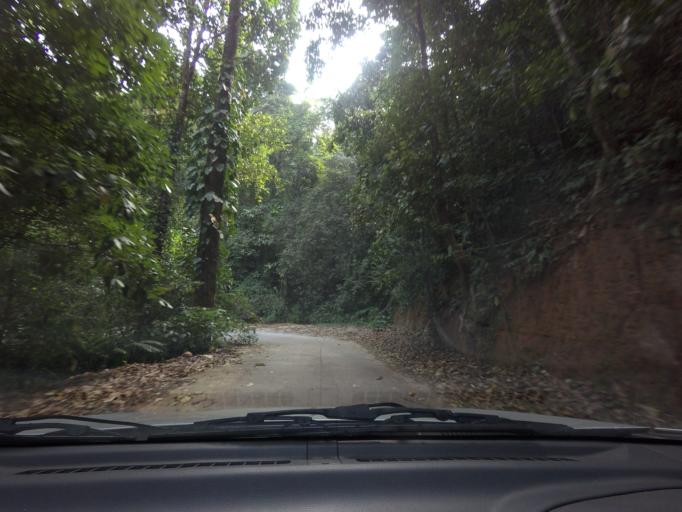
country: IN
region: Karnataka
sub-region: Kodagu
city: Somvarpet
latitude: 12.7236
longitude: 75.6627
